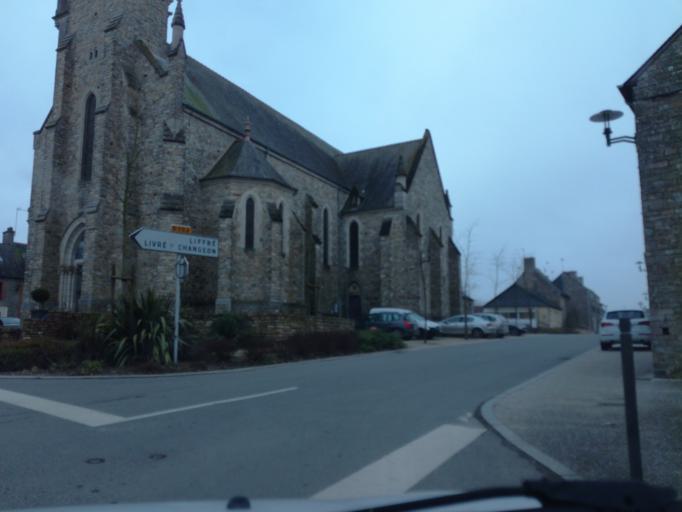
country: FR
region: Brittany
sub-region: Departement d'Ille-et-Vilaine
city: Gosne
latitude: 48.2462
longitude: -1.4630
